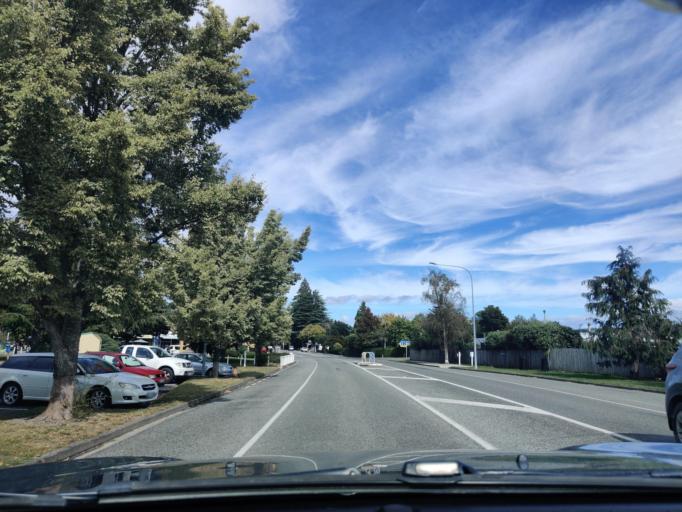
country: NZ
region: Tasman
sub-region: Tasman District
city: Wakefield
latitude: -41.4051
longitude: 173.0433
